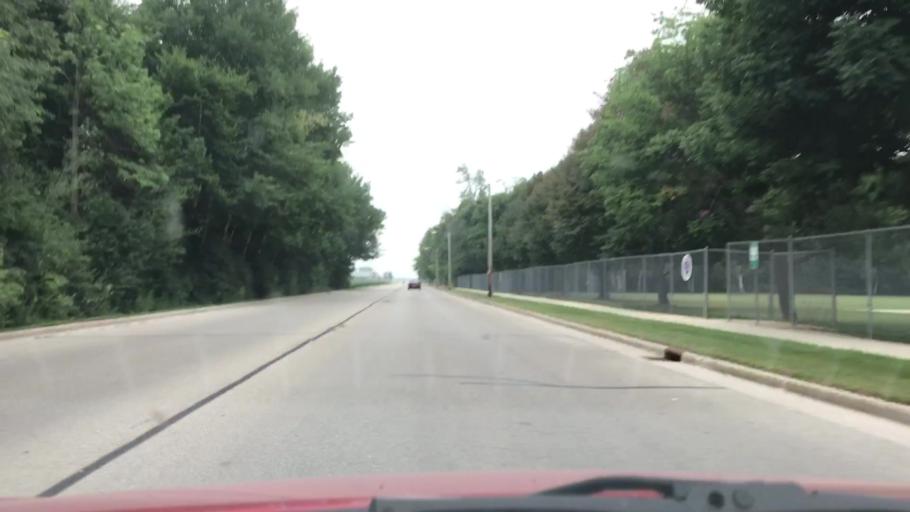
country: US
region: Wisconsin
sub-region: Outagamie County
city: Seymour
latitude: 44.5073
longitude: -88.3204
